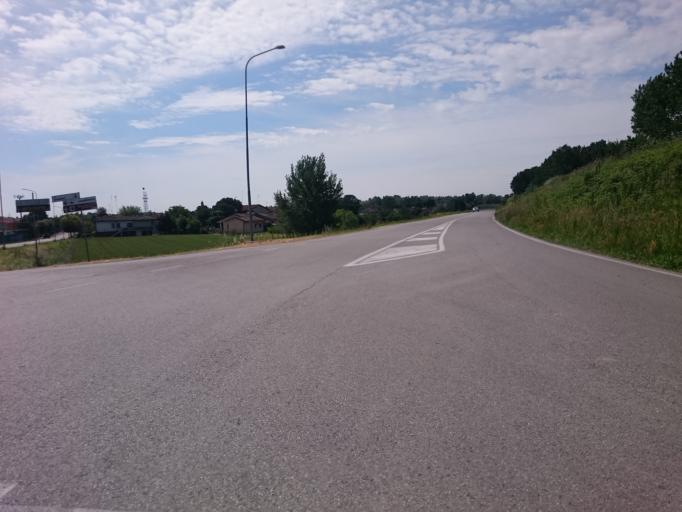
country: IT
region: Veneto
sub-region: Provincia di Rovigo
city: Ariano
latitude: 44.9522
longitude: 12.1201
